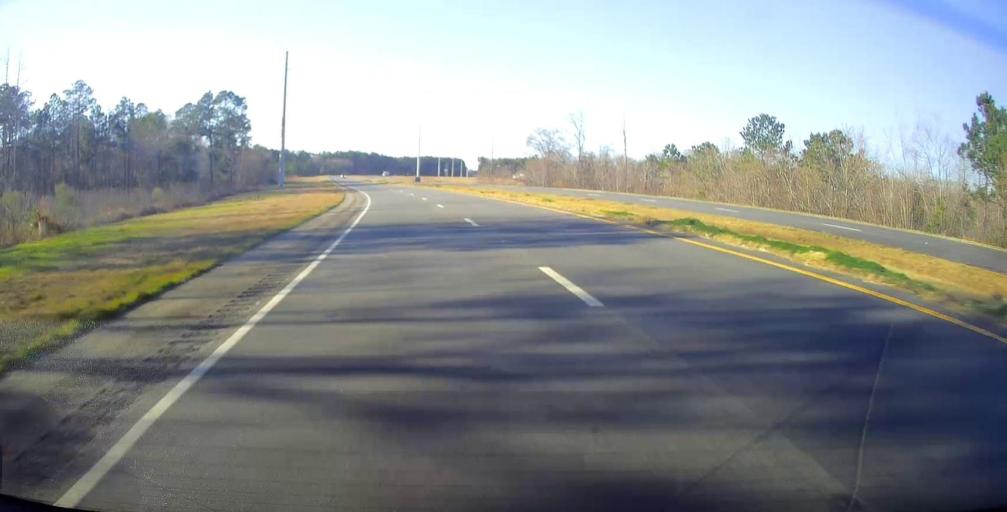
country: US
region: Georgia
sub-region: Lee County
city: Leesburg
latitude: 31.8114
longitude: -84.2100
